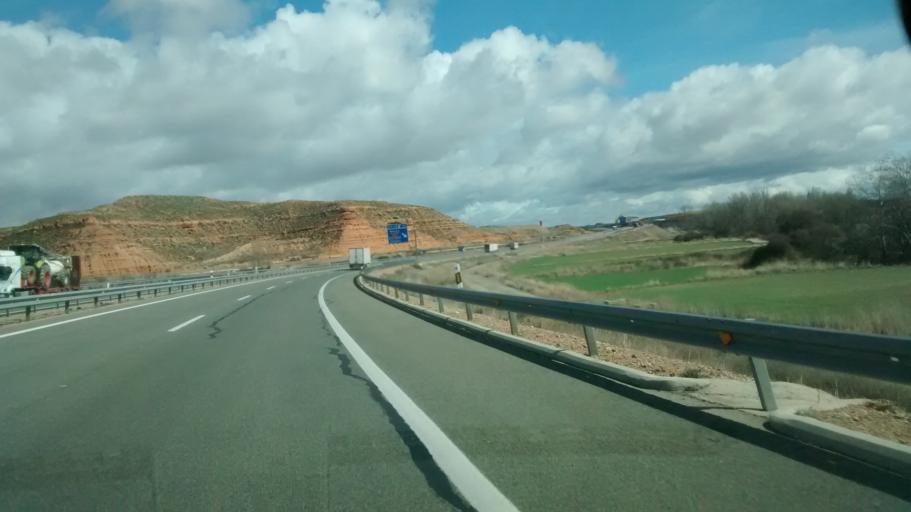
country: ES
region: Aragon
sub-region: Provincia de Zaragoza
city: Monreal de Ariza
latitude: 41.3057
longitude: -2.1394
